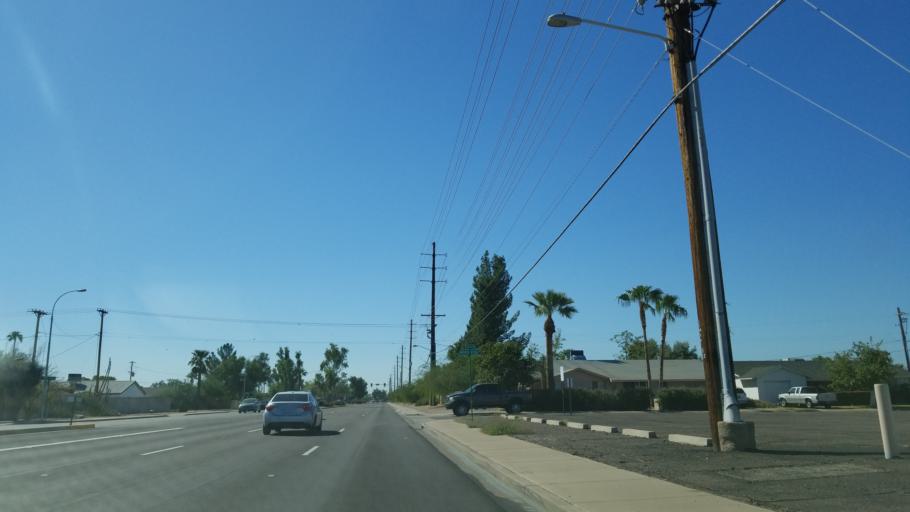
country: US
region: Arizona
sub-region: Maricopa County
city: Scottsdale
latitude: 33.4723
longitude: -111.9090
